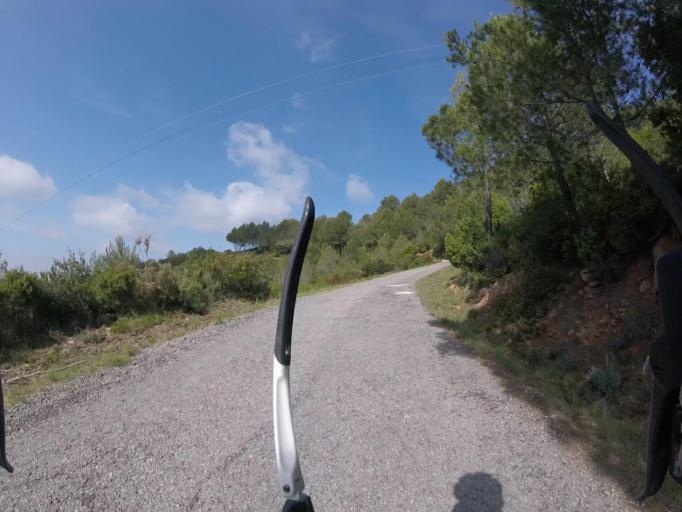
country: ES
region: Valencia
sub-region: Provincia de Castello
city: Benicassim
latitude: 40.0772
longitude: 0.0225
